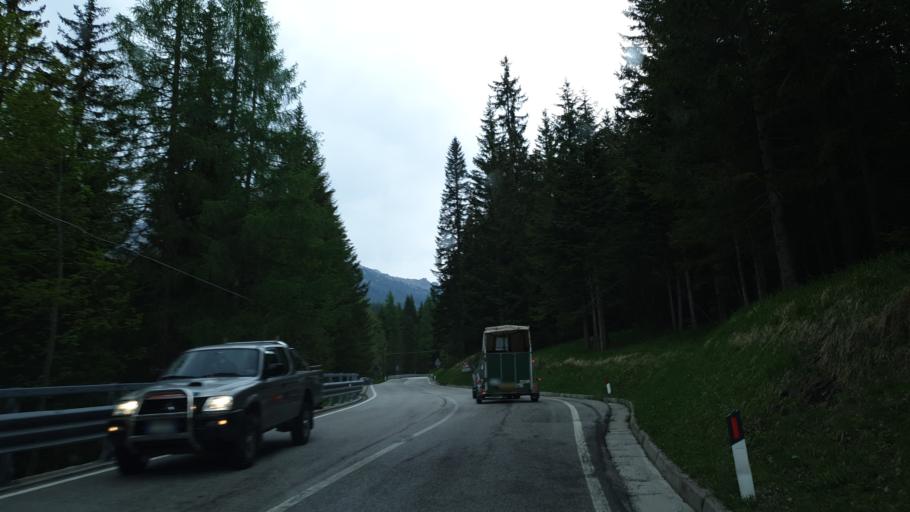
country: IT
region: Veneto
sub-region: Provincia di Belluno
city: San Vito
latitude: 46.5538
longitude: 12.2458
